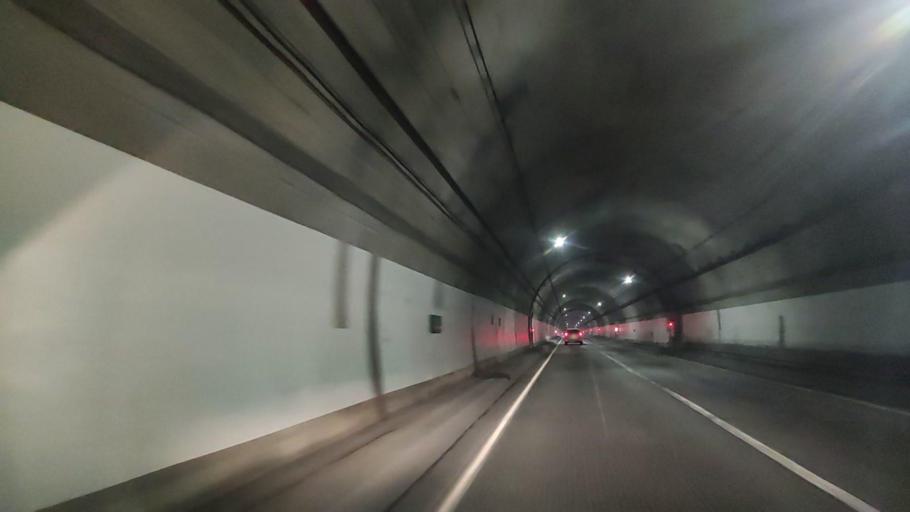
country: JP
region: Hokkaido
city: Rumoi
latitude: 43.7097
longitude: 141.3327
